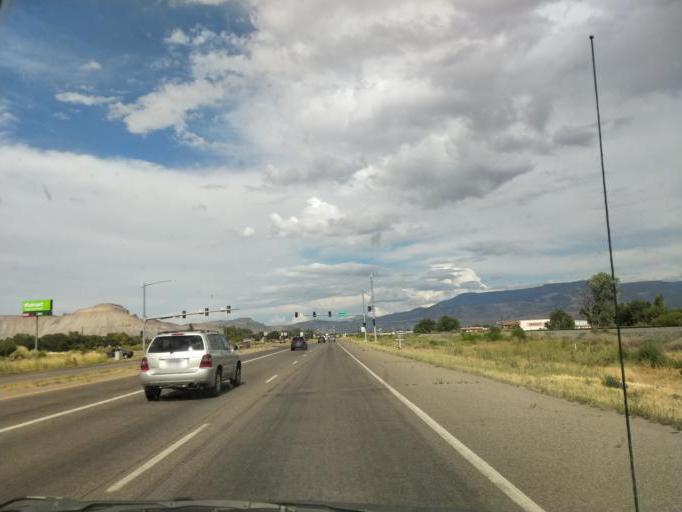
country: US
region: Colorado
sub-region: Mesa County
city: Fruitvale
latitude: 39.0825
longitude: -108.4743
